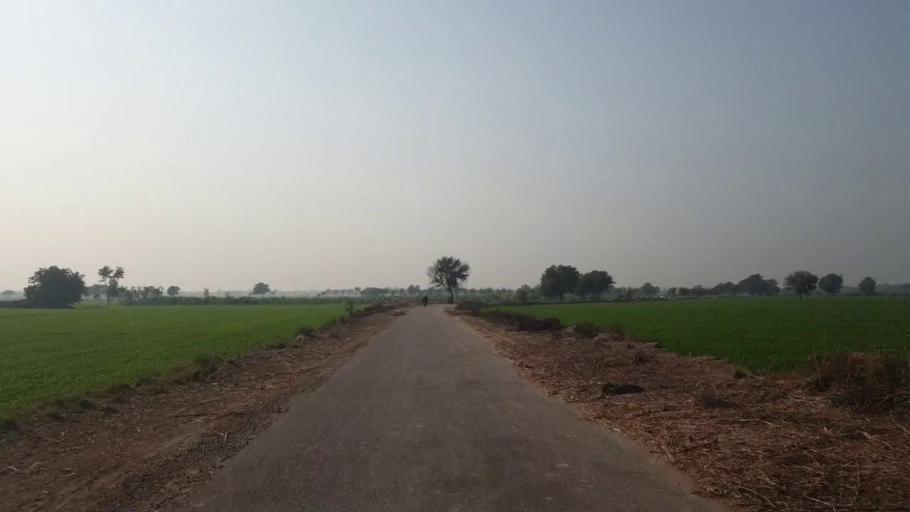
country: PK
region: Sindh
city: Shahdadpur
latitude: 25.9670
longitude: 68.5559
